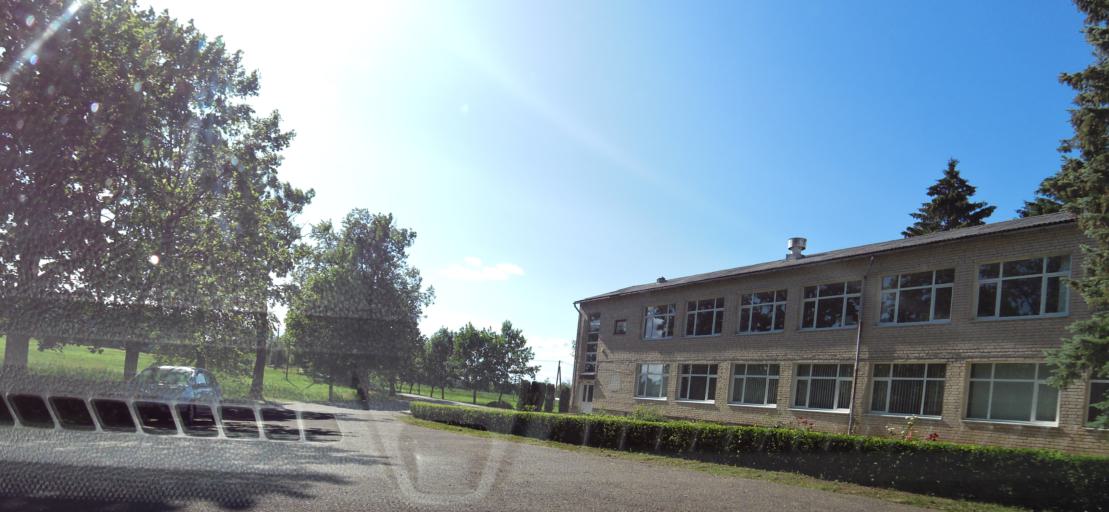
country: LT
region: Panevezys
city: Pasvalys
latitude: 56.1565
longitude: 24.4469
